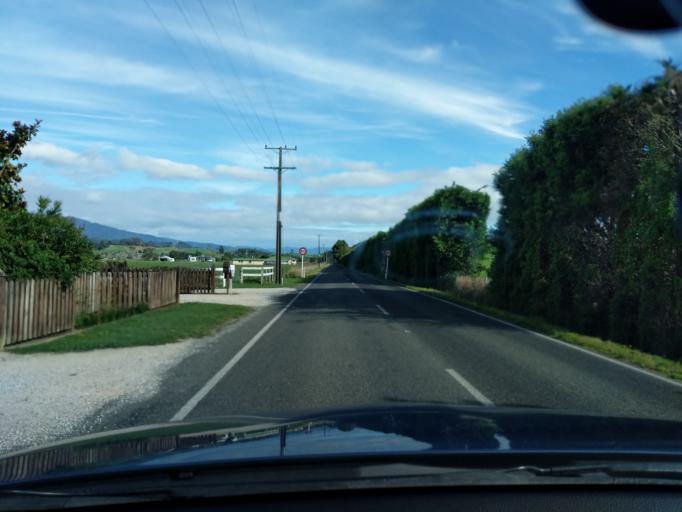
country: NZ
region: Tasman
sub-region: Tasman District
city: Takaka
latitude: -40.8540
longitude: 172.8463
